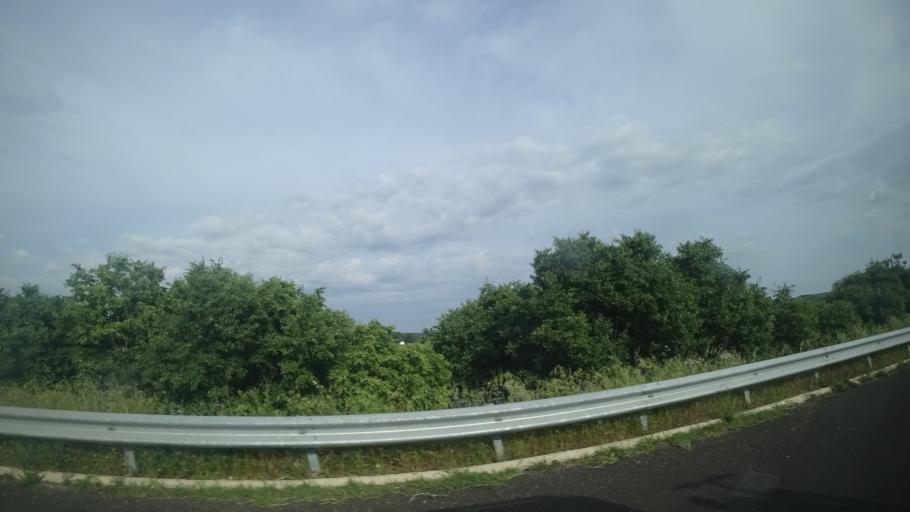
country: FR
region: Languedoc-Roussillon
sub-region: Departement de l'Herault
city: Lezignan-la-Cebe
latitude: 43.4754
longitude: 3.4370
